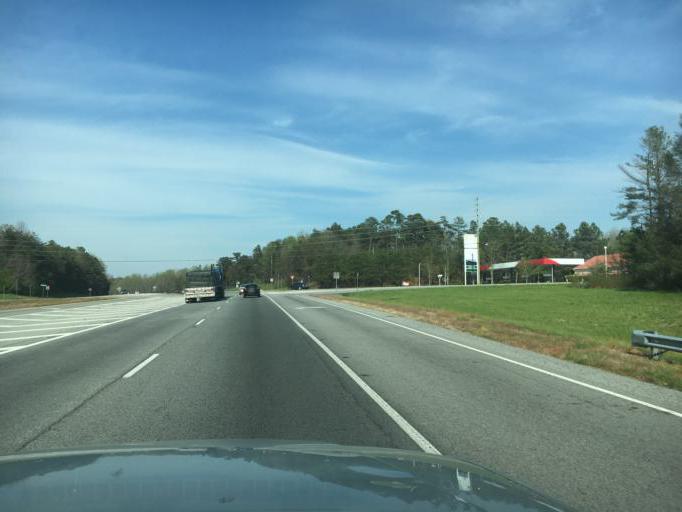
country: US
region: Georgia
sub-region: Habersham County
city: Raoul
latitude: 34.4352
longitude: -83.6328
